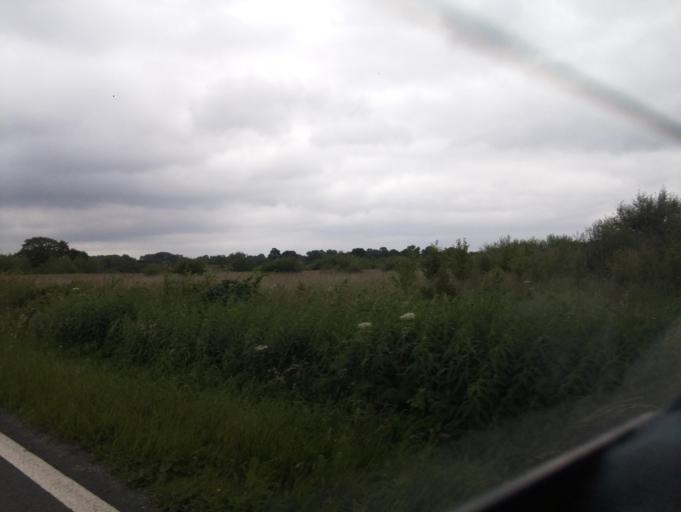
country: GB
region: England
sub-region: Staffordshire
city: Mayfield
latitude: 52.9605
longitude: -1.7582
